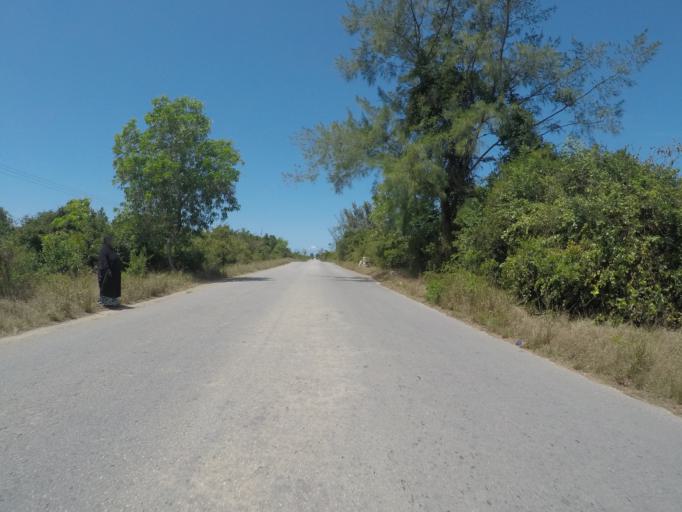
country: TZ
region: Zanzibar Central/South
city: Nganane
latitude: -6.2708
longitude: 39.5054
